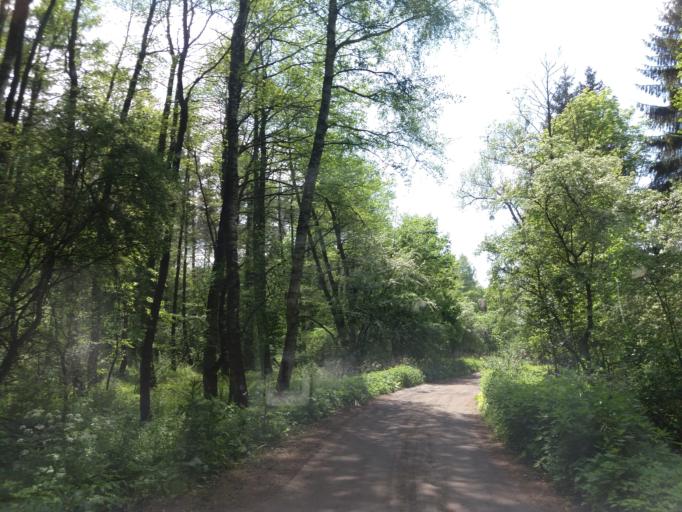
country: PL
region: West Pomeranian Voivodeship
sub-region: Powiat choszczenski
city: Recz
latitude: 53.2698
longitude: 15.5317
